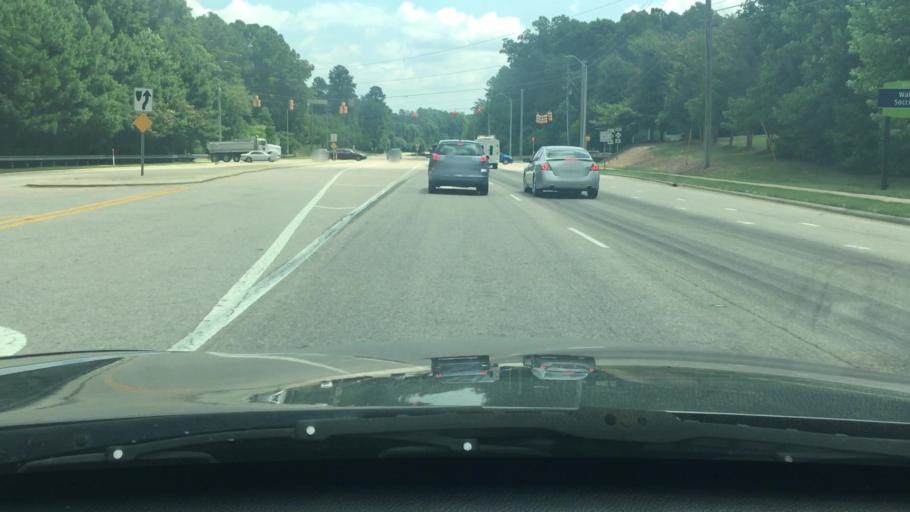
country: US
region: North Carolina
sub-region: Wake County
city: Cary
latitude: 35.7948
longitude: -78.7646
